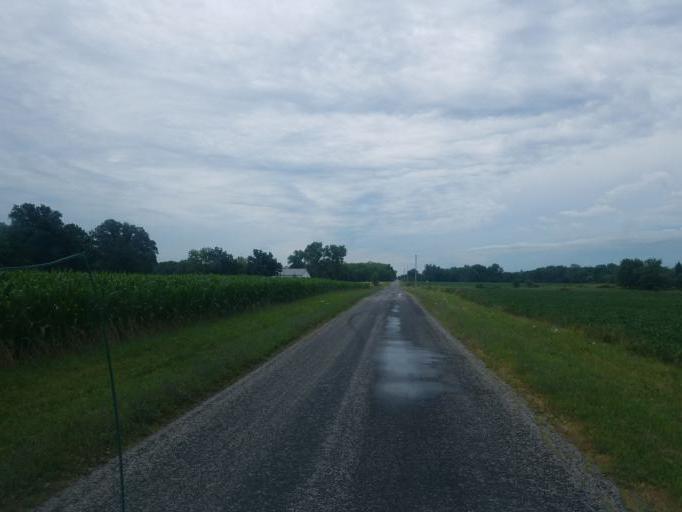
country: US
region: Ohio
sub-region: Paulding County
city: Antwerp
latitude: 41.2390
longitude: -84.7083
